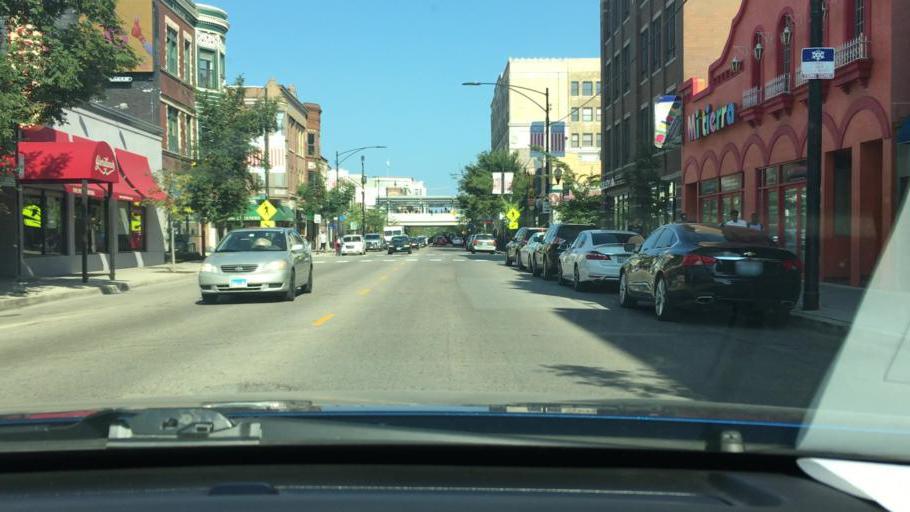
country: US
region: Illinois
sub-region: Cook County
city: Chicago
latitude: 41.9399
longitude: -87.6560
